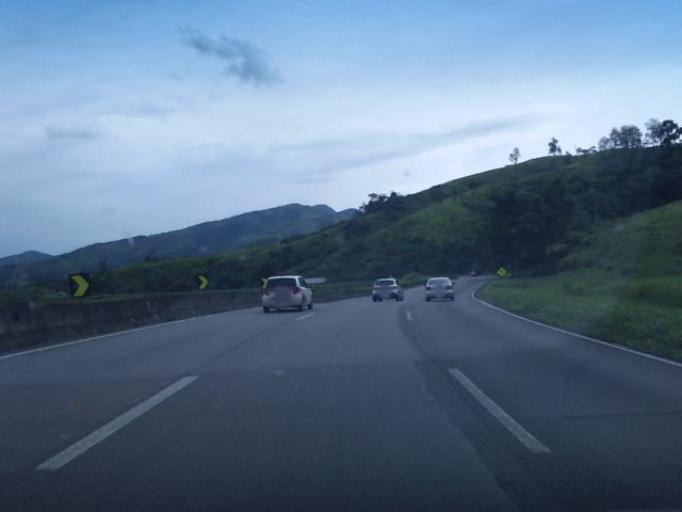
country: BR
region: Sao Paulo
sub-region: Cajati
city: Cajati
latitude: -24.7877
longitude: -48.2086
